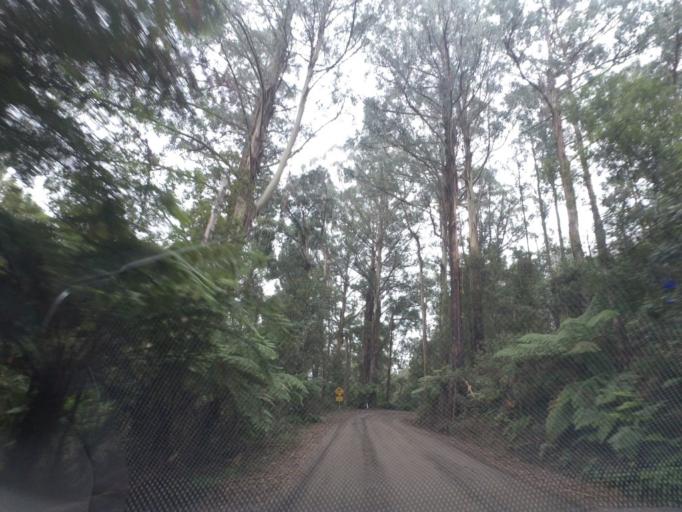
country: AU
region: Victoria
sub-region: Yarra Ranges
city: Launching Place
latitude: -37.7126
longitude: 145.5876
